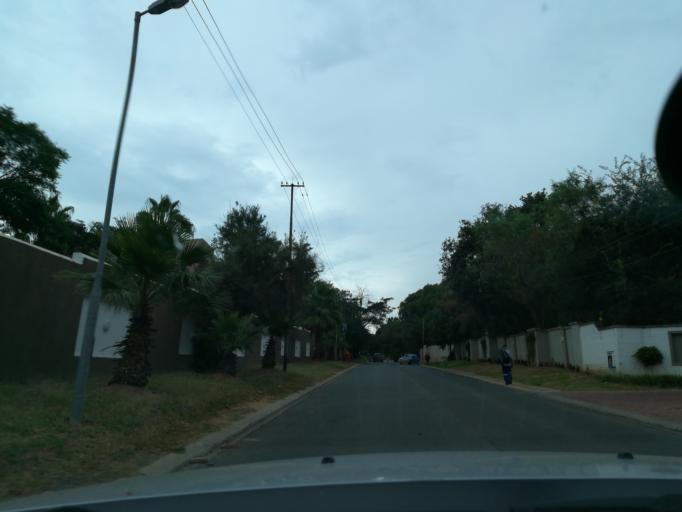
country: ZA
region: Gauteng
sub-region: City of Johannesburg Metropolitan Municipality
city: Diepsloot
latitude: -26.0691
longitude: 27.9978
